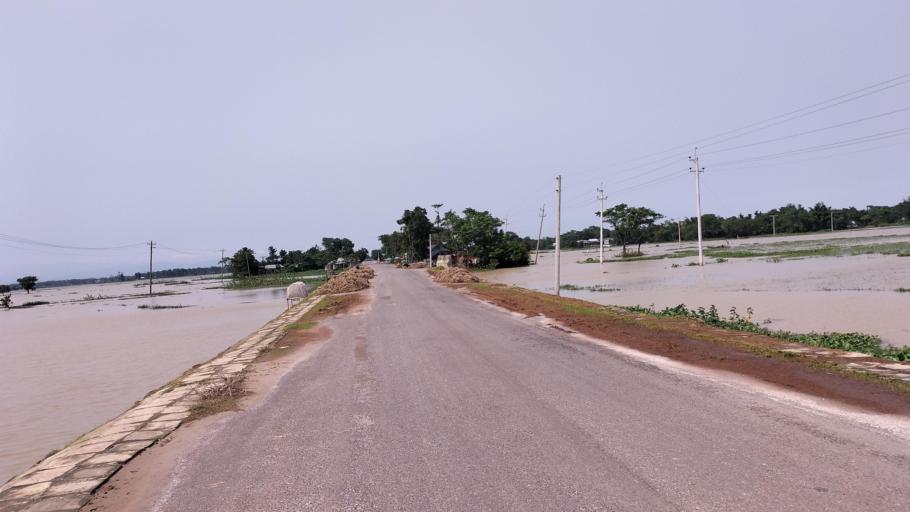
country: BD
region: Dhaka
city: Netrakona
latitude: 25.0138
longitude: 90.8538
